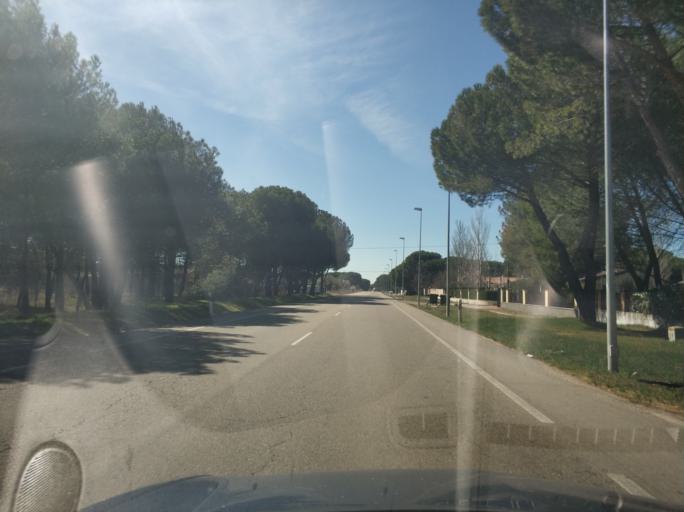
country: ES
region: Castille and Leon
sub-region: Provincia de Valladolid
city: Tudela de Duero
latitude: 41.5740
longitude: -4.5842
